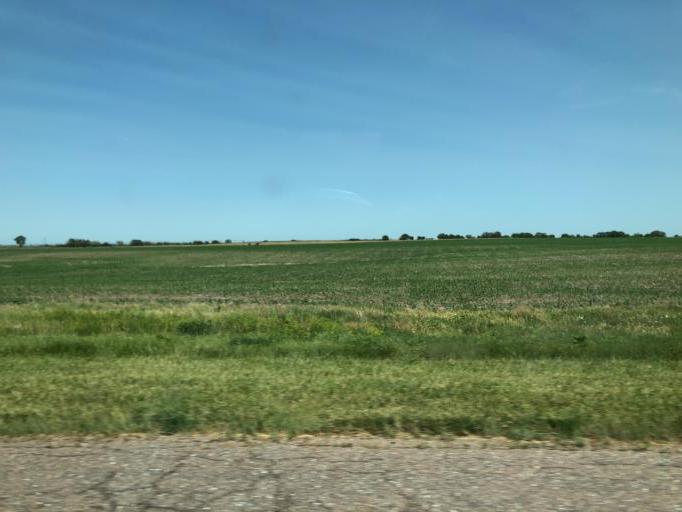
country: US
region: Nebraska
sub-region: Thayer County
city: Hebron
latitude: 40.3021
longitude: -97.5765
